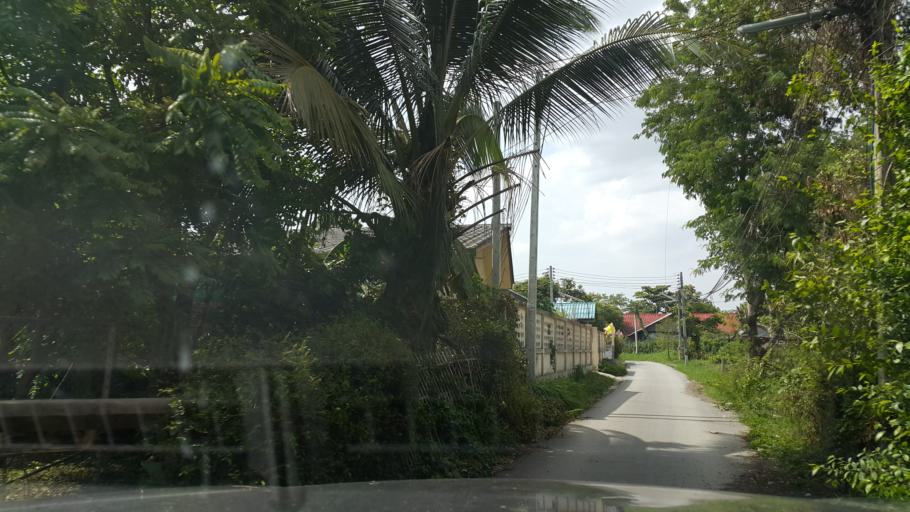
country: TH
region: Chiang Mai
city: San Kamphaeng
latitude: 18.7352
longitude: 99.1237
